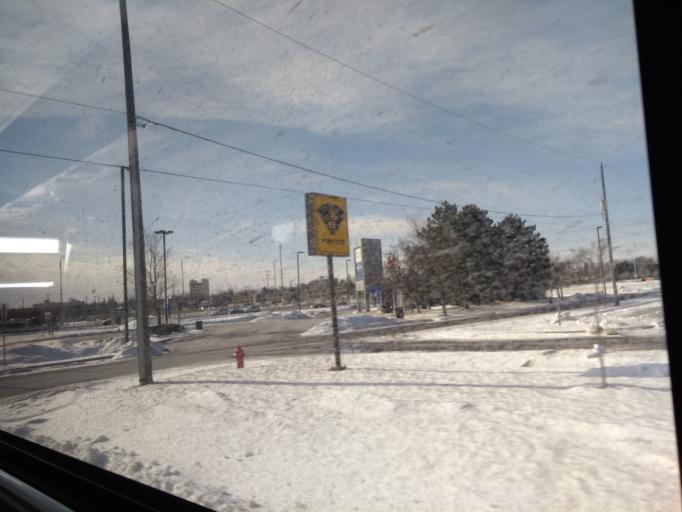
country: CA
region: Ontario
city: Niagara Falls
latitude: 43.0973
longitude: -79.0855
